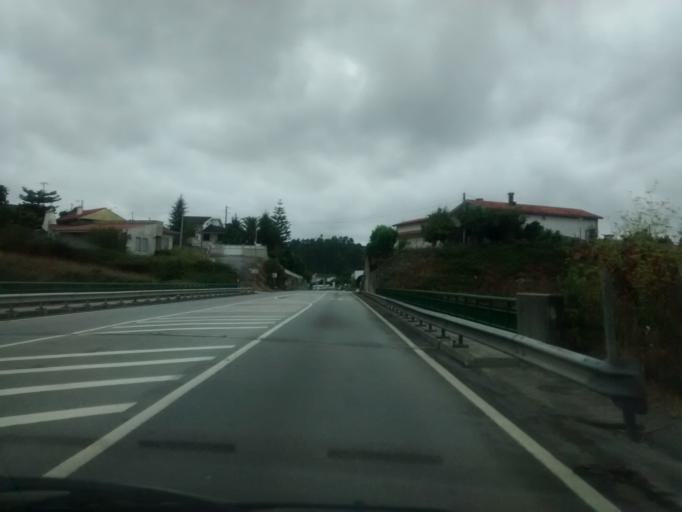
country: PT
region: Braga
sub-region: Braga
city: Oliveira
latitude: 41.4929
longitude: -8.4643
